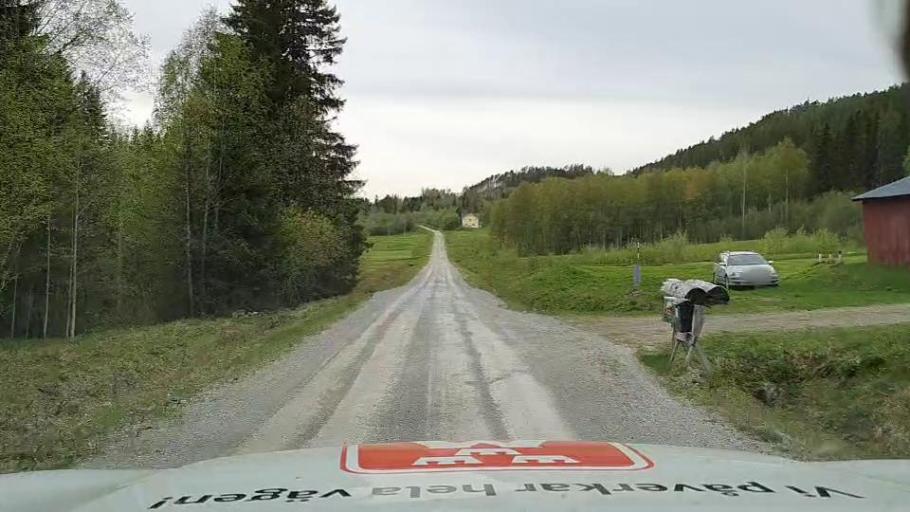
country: SE
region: Jaemtland
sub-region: Bergs Kommun
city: Hoverberg
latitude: 62.6654
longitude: 14.8217
